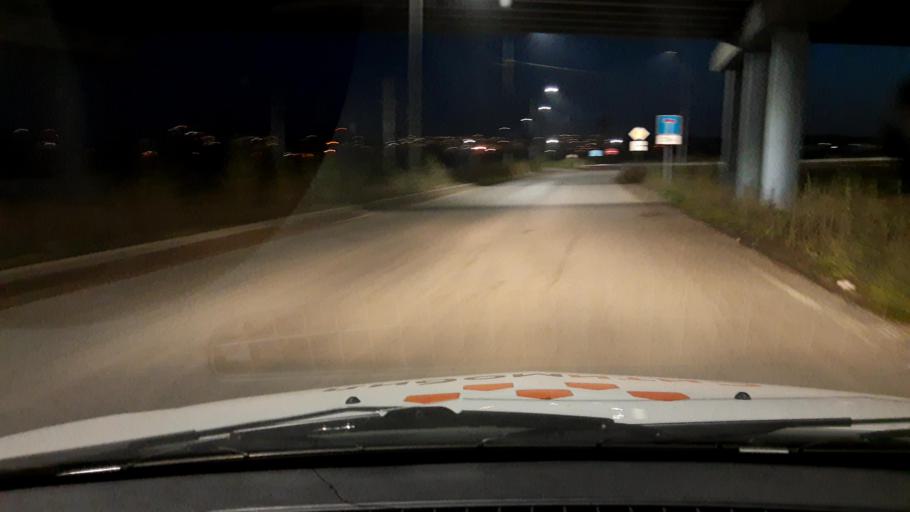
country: RU
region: Bashkortostan
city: Ufa
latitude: 54.8285
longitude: 56.1252
